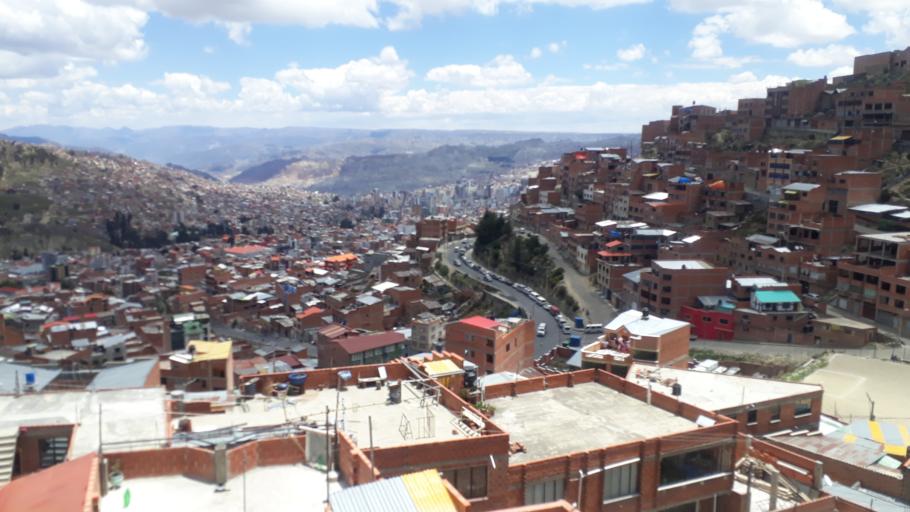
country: BO
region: La Paz
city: La Paz
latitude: -16.4680
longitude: -68.1223
